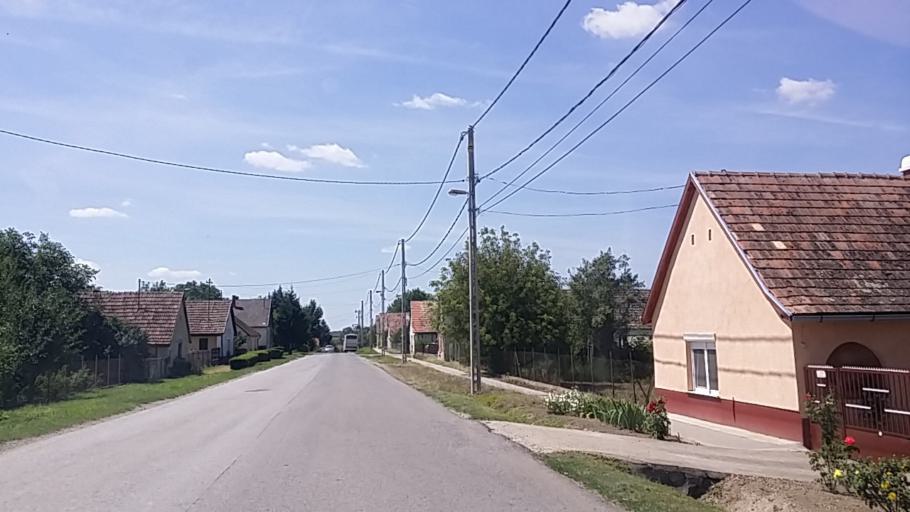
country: HU
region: Fejer
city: Deg
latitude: 46.8619
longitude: 18.4352
